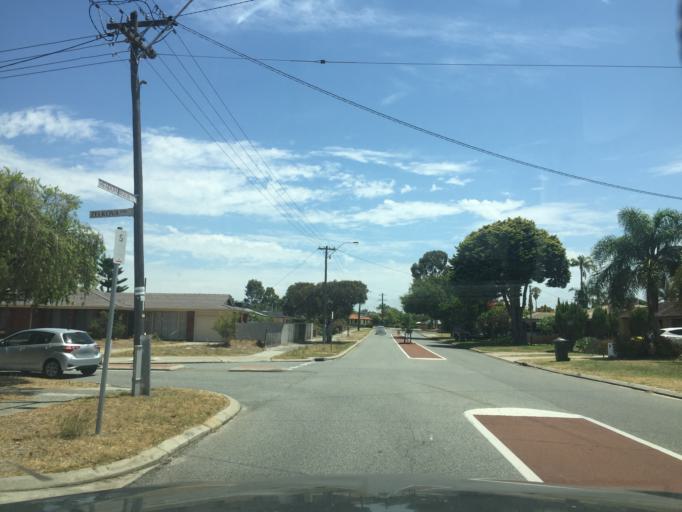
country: AU
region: Western Australia
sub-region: Canning
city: Ferndale
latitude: -32.0419
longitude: 115.9129
